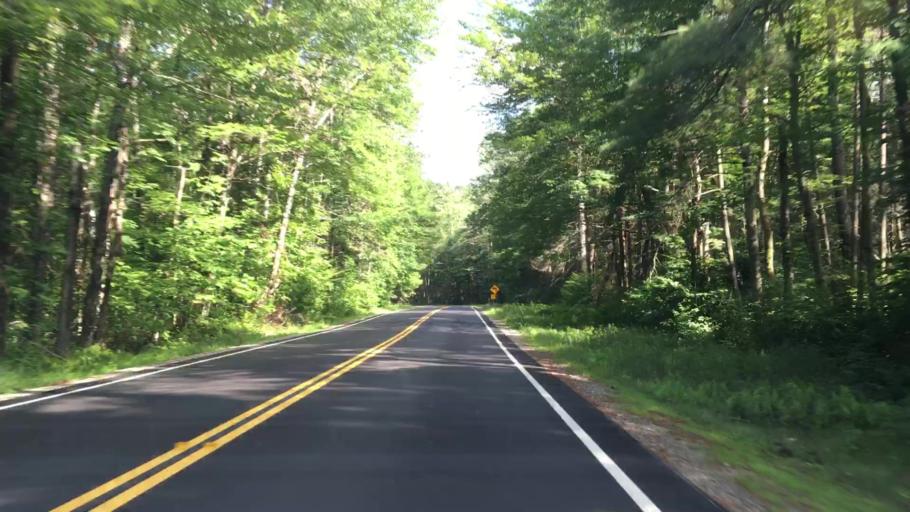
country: US
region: New Hampshire
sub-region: Grafton County
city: North Haverhill
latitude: 44.1012
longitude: -71.8623
